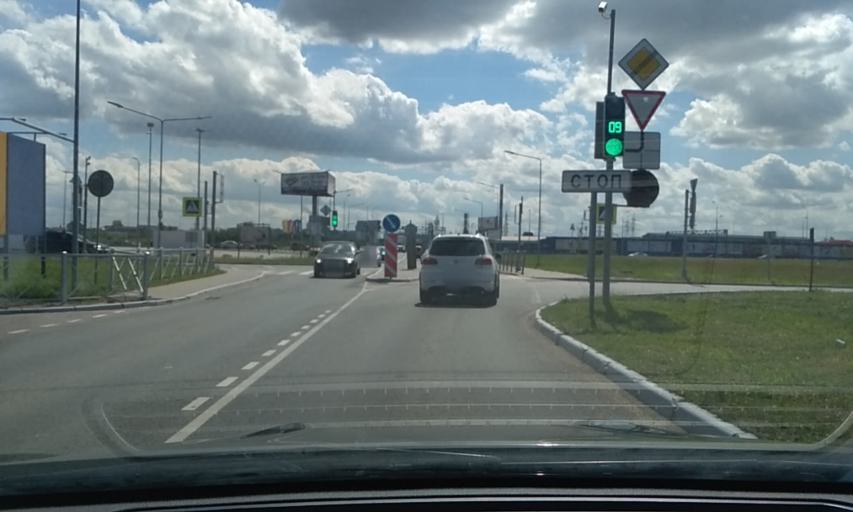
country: RU
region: Leningrad
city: Rybatskoye
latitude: 59.8916
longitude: 30.5087
